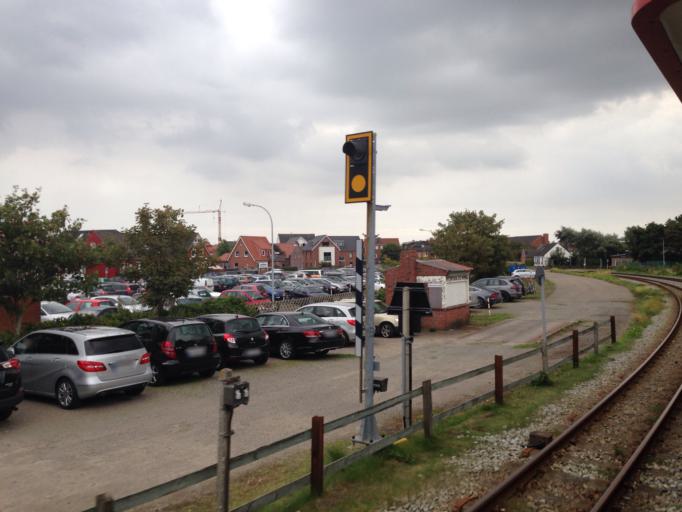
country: DE
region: Lower Saxony
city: Borkum
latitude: 53.5852
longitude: 6.6619
